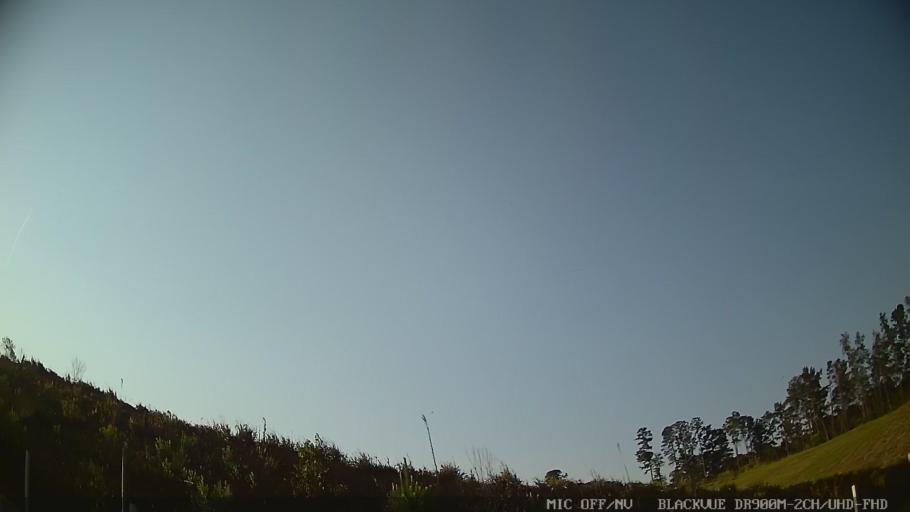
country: BR
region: Sao Paulo
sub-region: Itatiba
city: Itatiba
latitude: -23.0270
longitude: -46.8297
